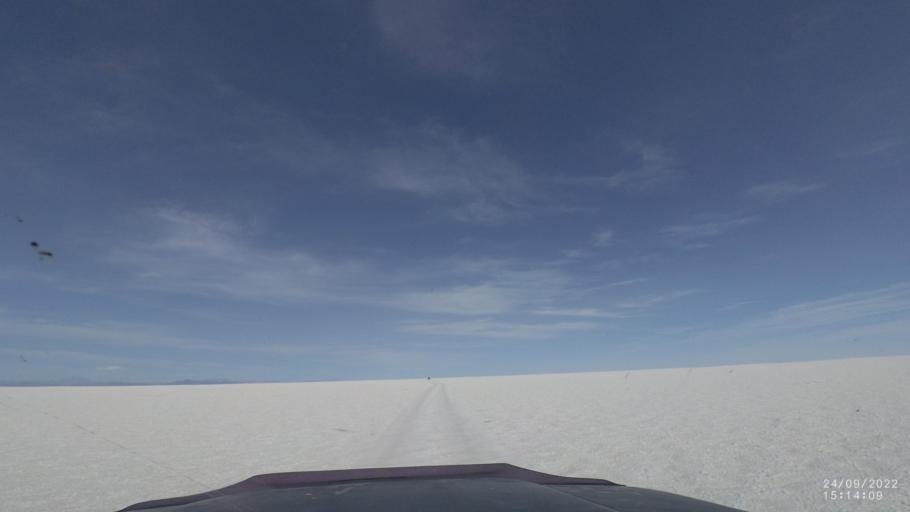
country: BO
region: Potosi
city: Colchani
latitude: -19.9616
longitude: -67.4584
